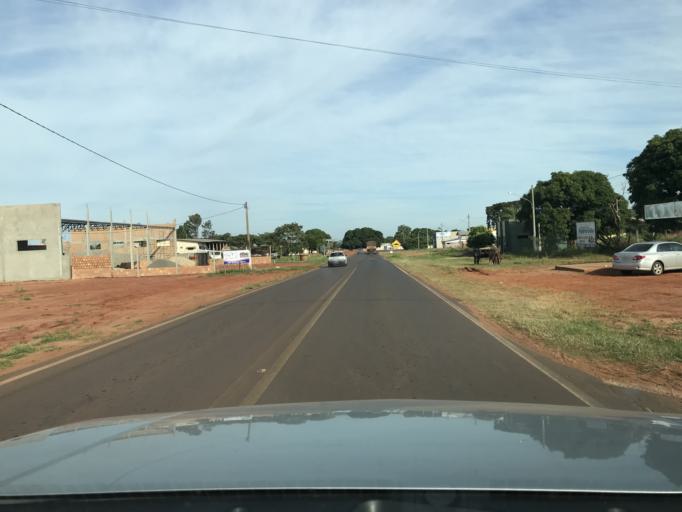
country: BR
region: Mato Grosso do Sul
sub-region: Iguatemi
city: Iguatemi
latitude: -23.6625
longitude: -54.5636
